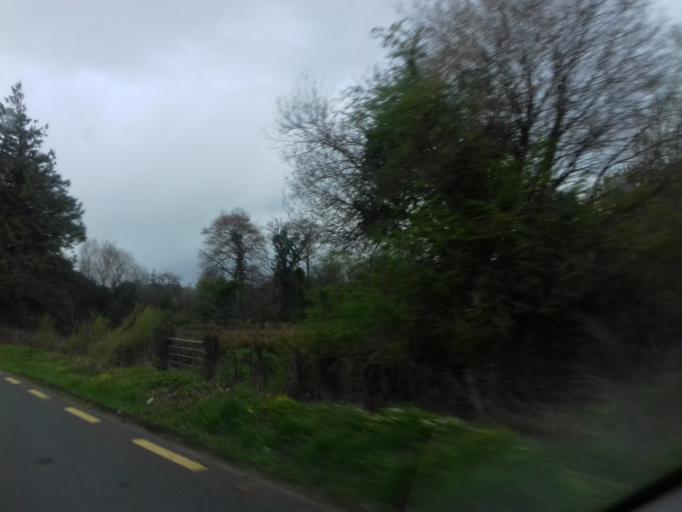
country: IE
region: Ulster
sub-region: An Cabhan
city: Ballyconnell
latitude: 54.1481
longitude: -7.7081
